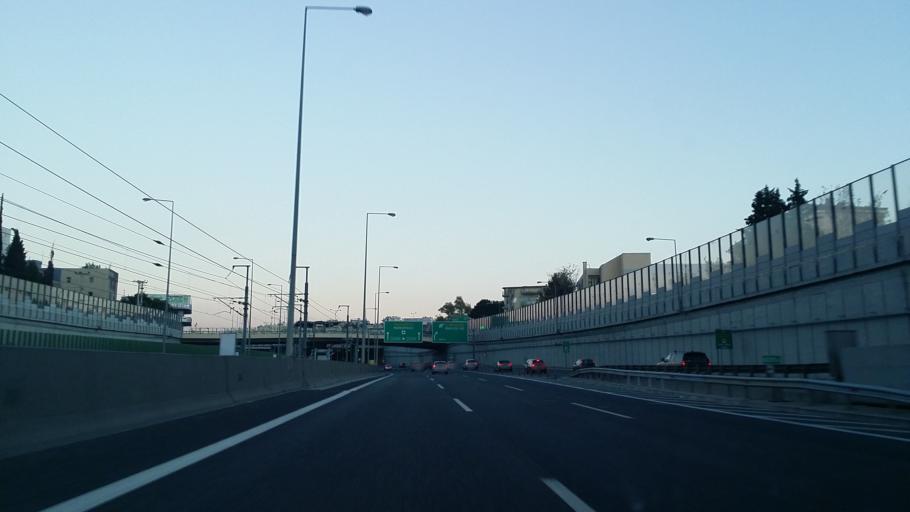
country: GR
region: Attica
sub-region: Nomarchia Athinas
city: Metamorfosi
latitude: 38.0609
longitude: 23.7526
